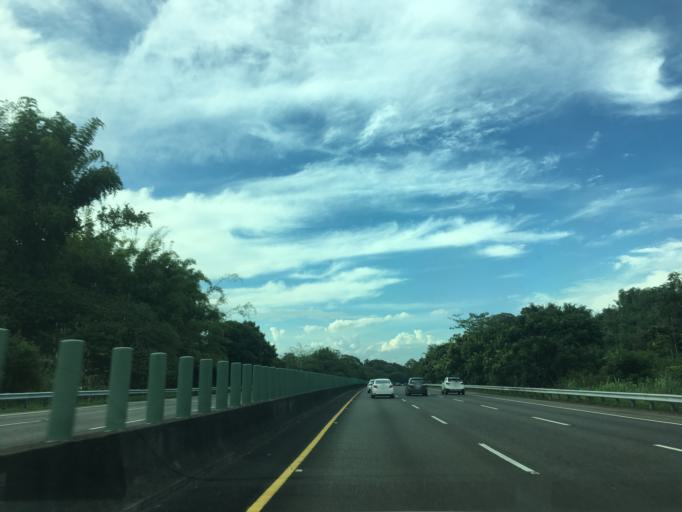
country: TW
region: Taiwan
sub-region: Chiayi
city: Jiayi Shi
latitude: 23.5642
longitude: 120.5051
